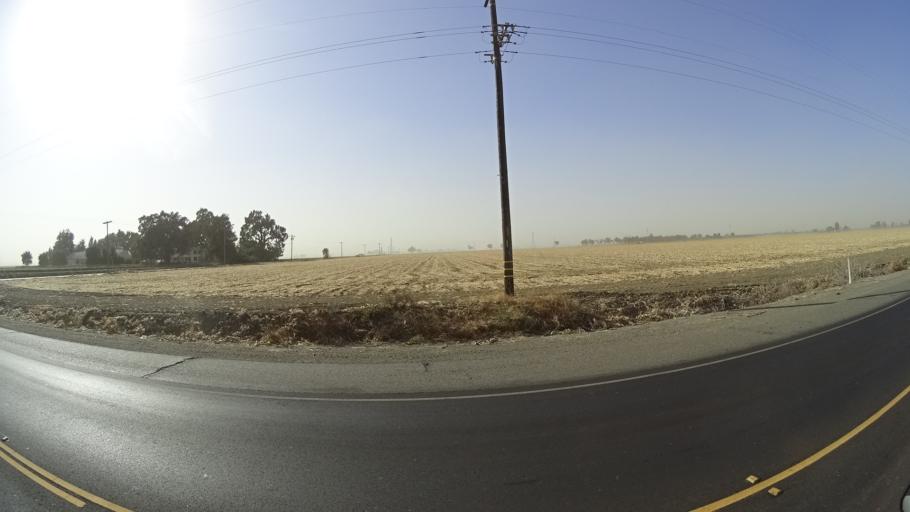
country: US
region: California
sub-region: Yolo County
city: Woodland
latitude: 38.7786
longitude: -121.7282
